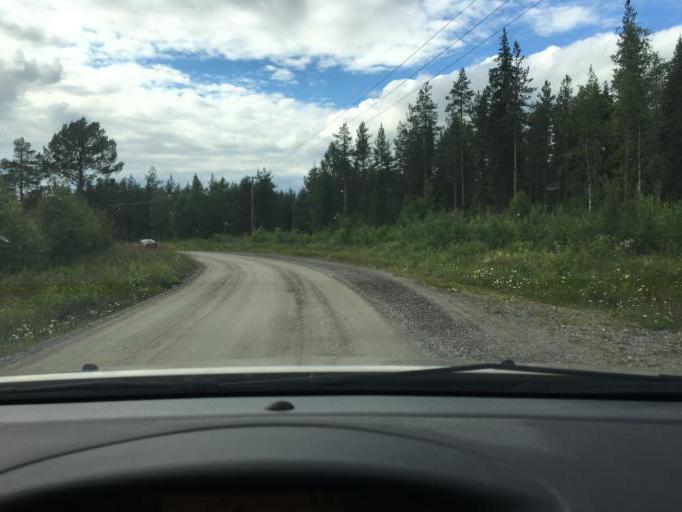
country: SE
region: Norrbotten
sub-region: Overkalix Kommun
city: OEverkalix
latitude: 66.0917
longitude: 22.8308
